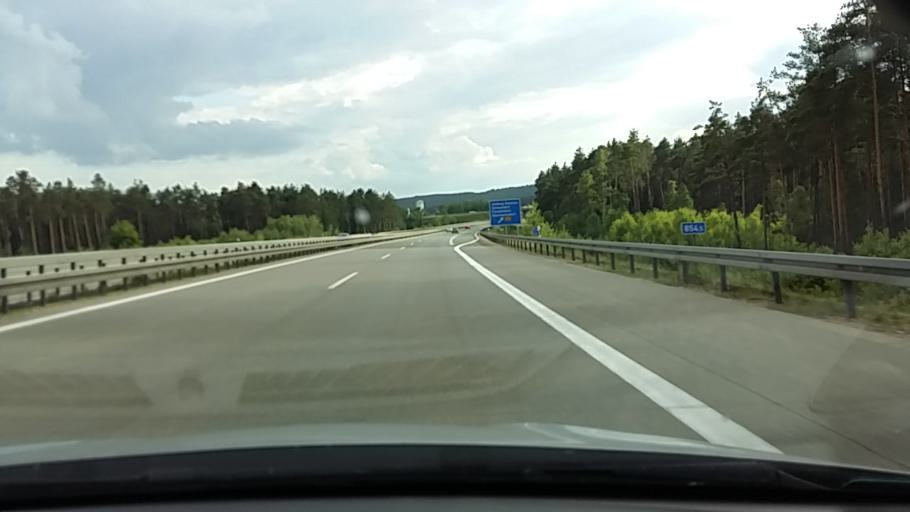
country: DE
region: Bavaria
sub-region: Upper Palatinate
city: Ebermannsdorf
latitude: 49.4046
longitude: 11.9850
